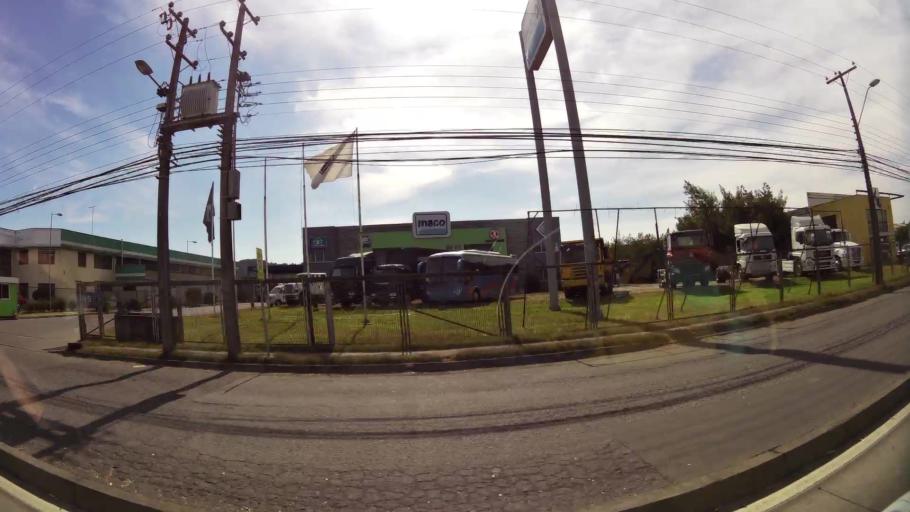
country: CL
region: Biobio
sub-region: Provincia de Concepcion
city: Talcahuano
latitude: -36.7660
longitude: -73.1164
